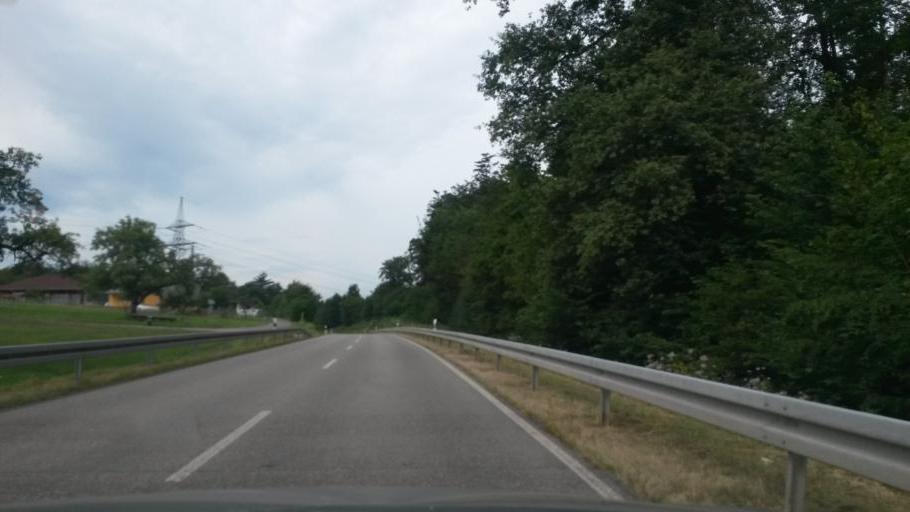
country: DE
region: Baden-Wuerttemberg
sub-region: Karlsruhe Region
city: Konigsbach-Stein
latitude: 48.9222
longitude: 8.5140
